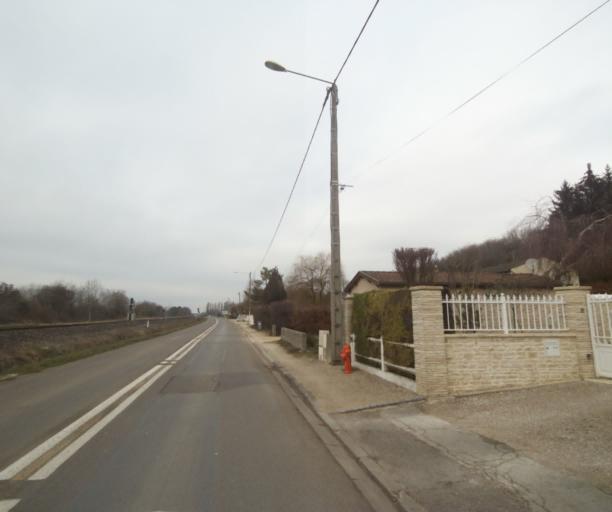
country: FR
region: Champagne-Ardenne
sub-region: Departement de la Haute-Marne
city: Bettancourt-la-Ferree
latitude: 48.6321
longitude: 4.9846
